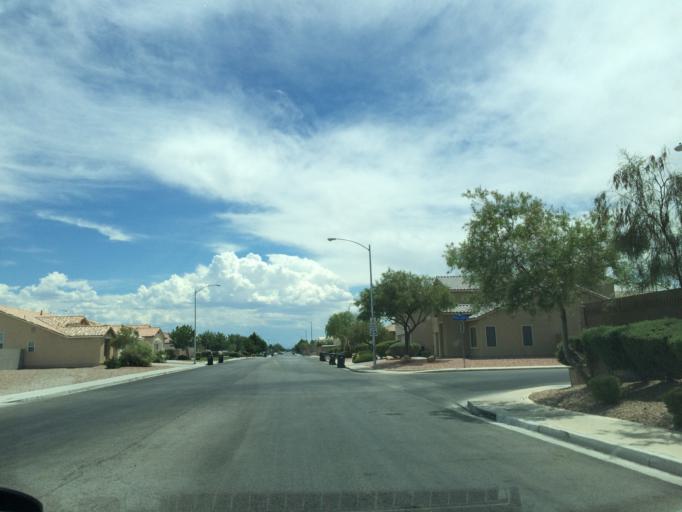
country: US
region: Nevada
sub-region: Clark County
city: North Las Vegas
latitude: 36.2608
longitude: -115.1846
